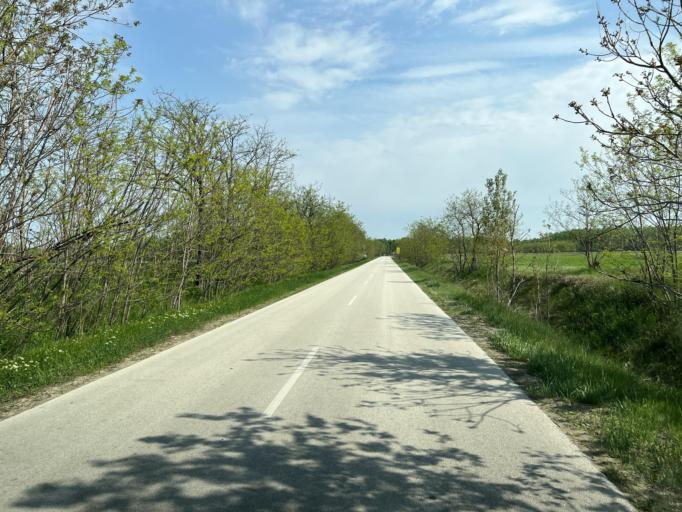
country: HU
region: Pest
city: Kocser
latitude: 47.0481
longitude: 19.9445
